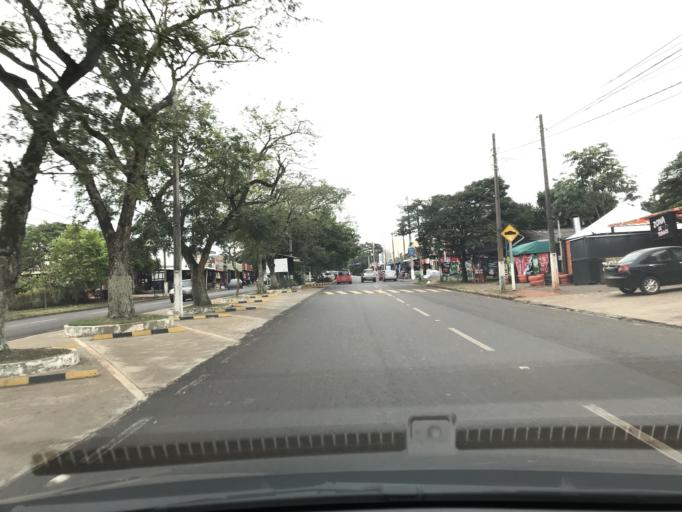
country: PY
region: Canindeyu
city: Salto del Guaira
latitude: -24.0525
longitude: -54.3061
